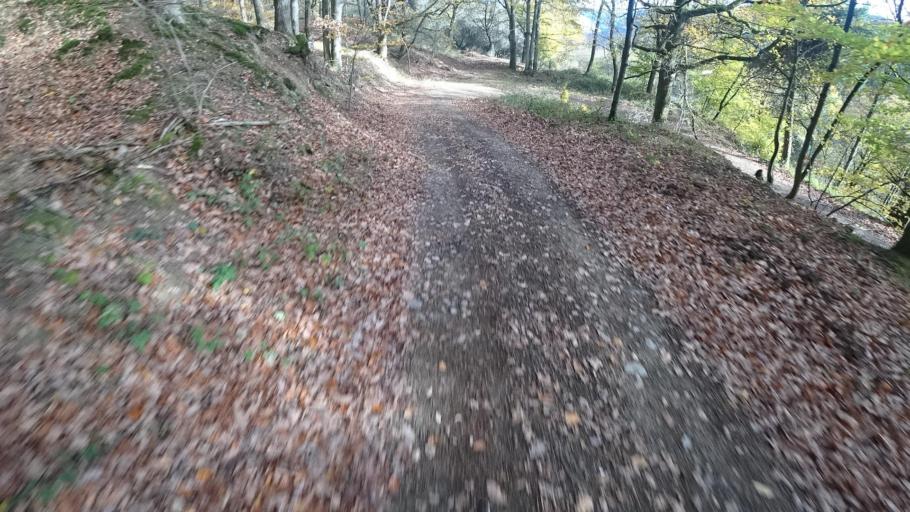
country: DE
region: Rheinland-Pfalz
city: Honningen
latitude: 50.4837
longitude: 6.9514
